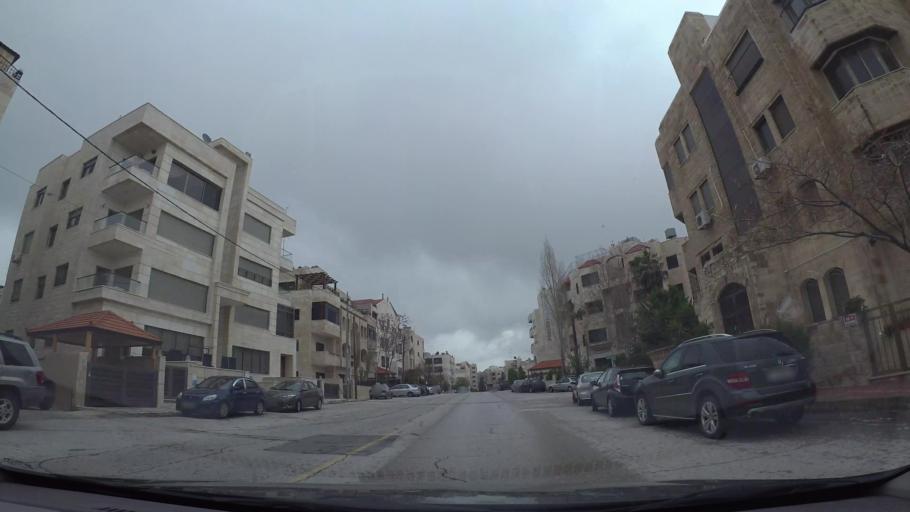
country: JO
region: Amman
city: Wadi as Sir
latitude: 31.9486
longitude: 35.8687
